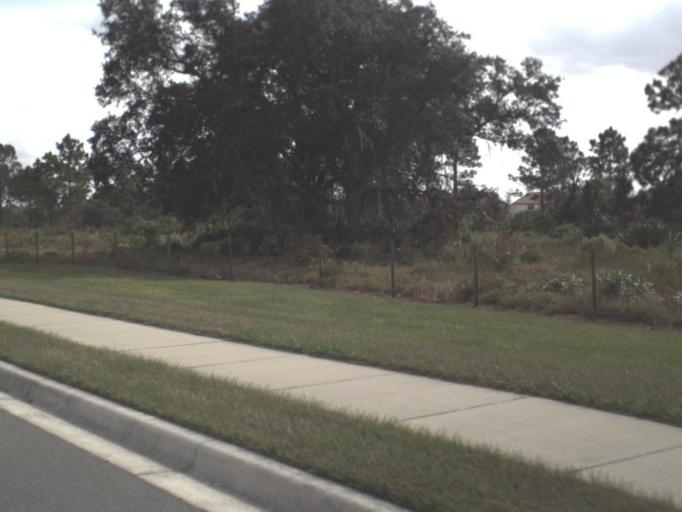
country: US
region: Florida
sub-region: Osceola County
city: Saint Cloud
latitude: 28.3546
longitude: -81.2388
